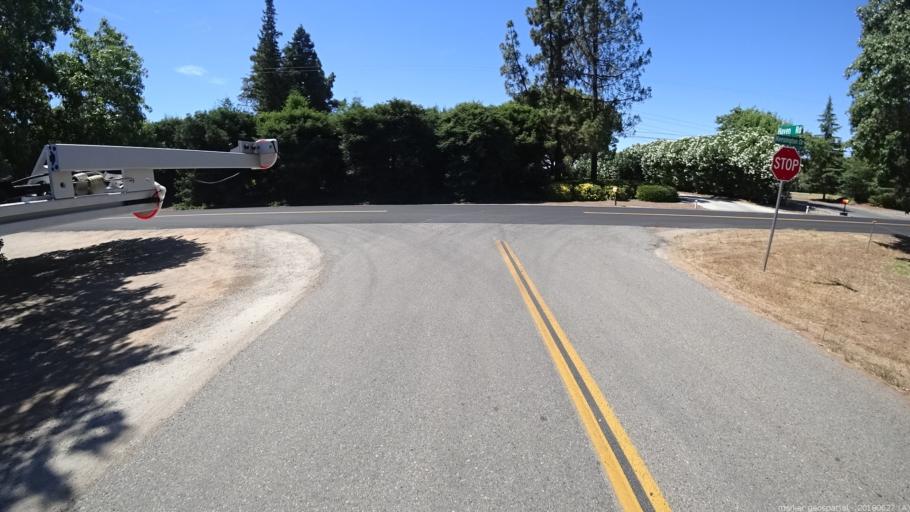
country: US
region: California
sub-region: Madera County
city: Bonadelle Ranchos-Madera Ranchos
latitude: 36.9180
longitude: -119.8897
